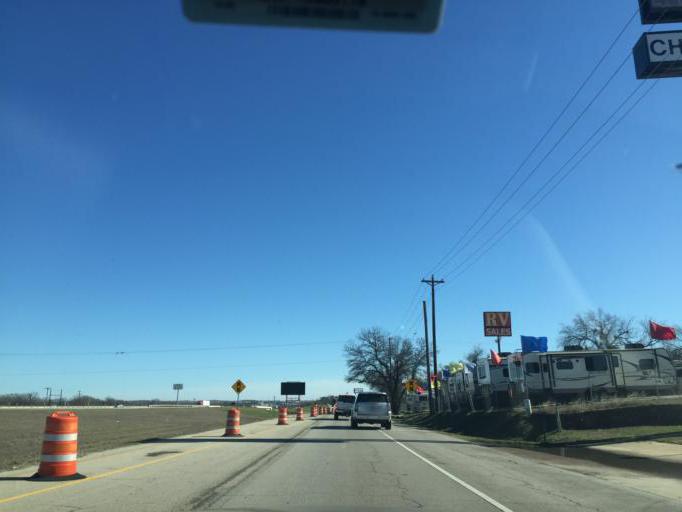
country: US
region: Texas
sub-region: Parker County
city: Willow Park
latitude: 32.7483
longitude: -97.6775
